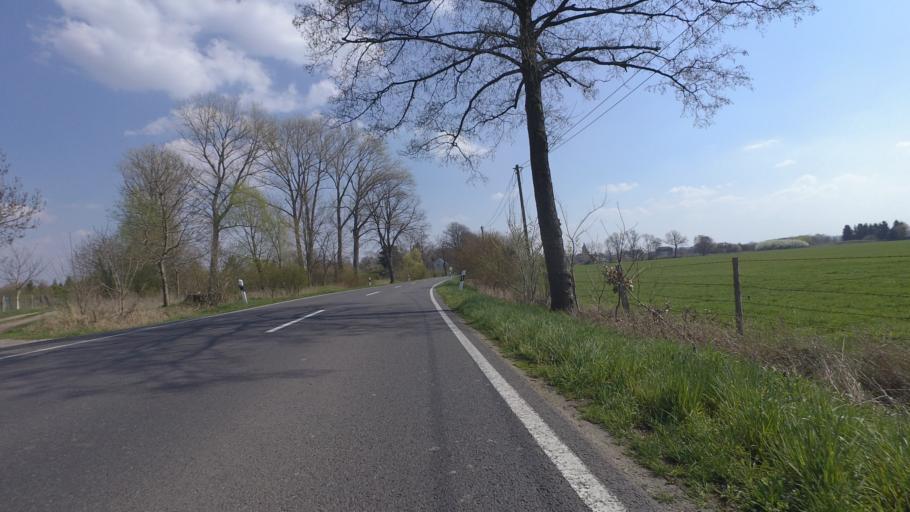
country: DE
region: Brandenburg
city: Mittenwalde
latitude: 52.2714
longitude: 13.5222
